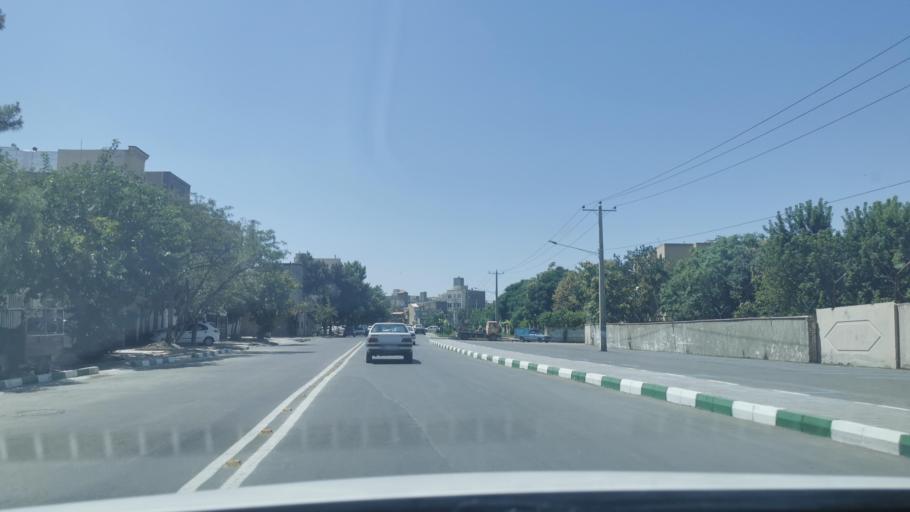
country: IR
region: Razavi Khorasan
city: Mashhad
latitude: 36.2752
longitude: 59.5788
